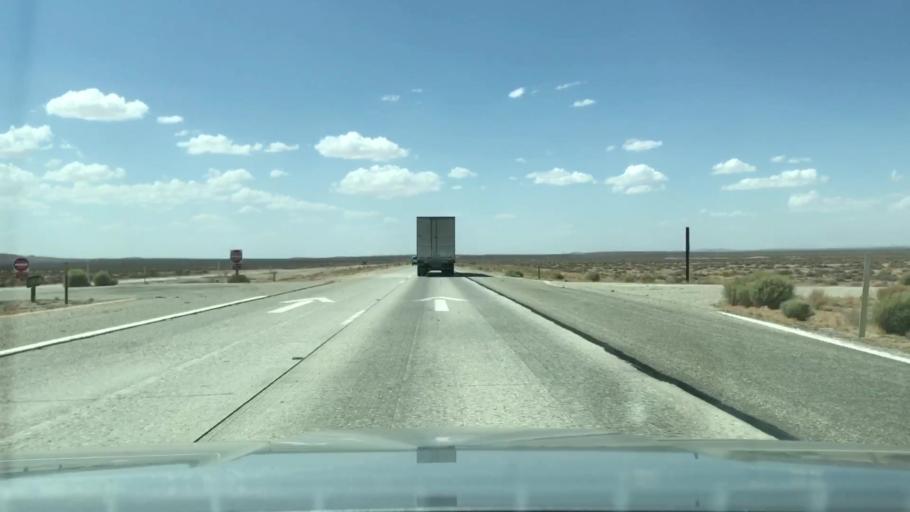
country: US
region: California
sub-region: San Bernardino County
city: Lenwood
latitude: 34.9290
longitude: -117.3540
